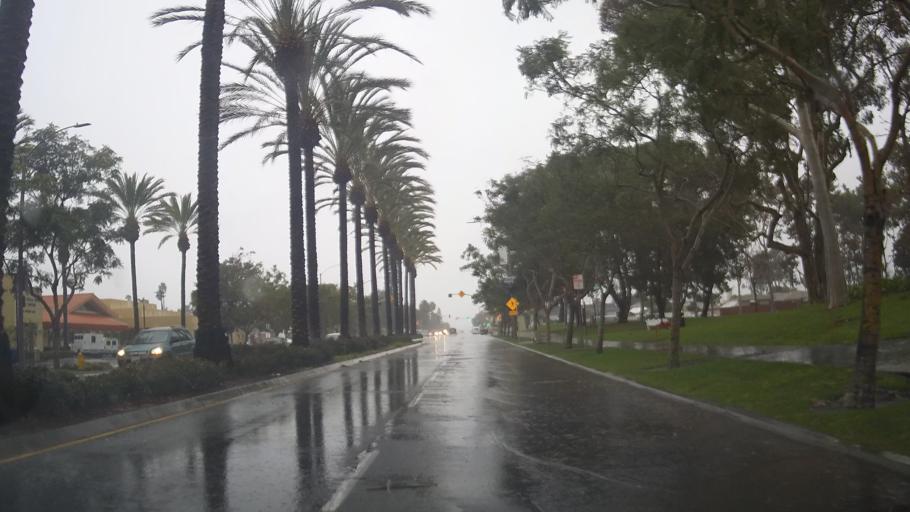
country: US
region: California
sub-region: San Diego County
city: Chula Vista
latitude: 32.6405
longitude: -117.0836
